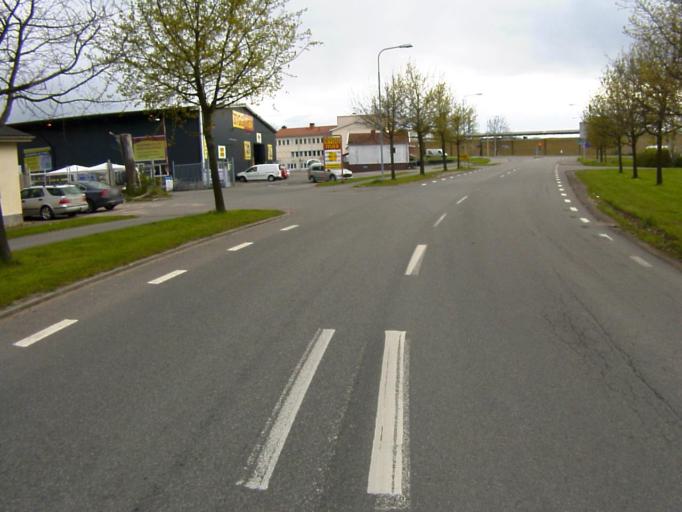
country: SE
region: Skane
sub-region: Kristianstads Kommun
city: Kristianstad
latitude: 56.0437
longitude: 14.1581
